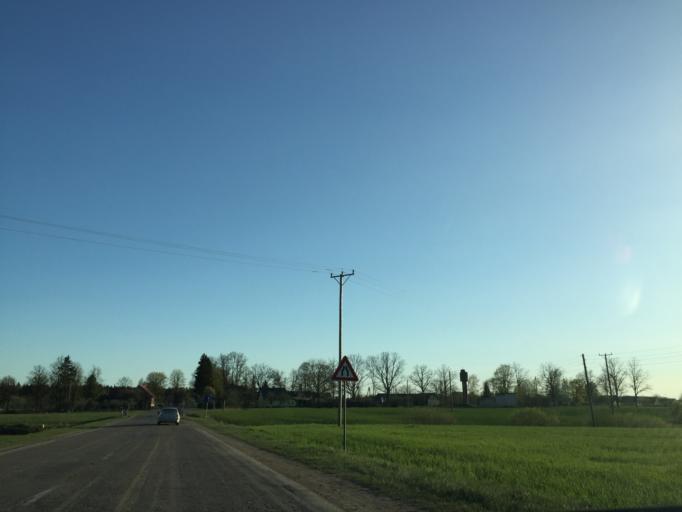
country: LV
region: Koknese
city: Koknese
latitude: 56.6788
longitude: 25.4829
